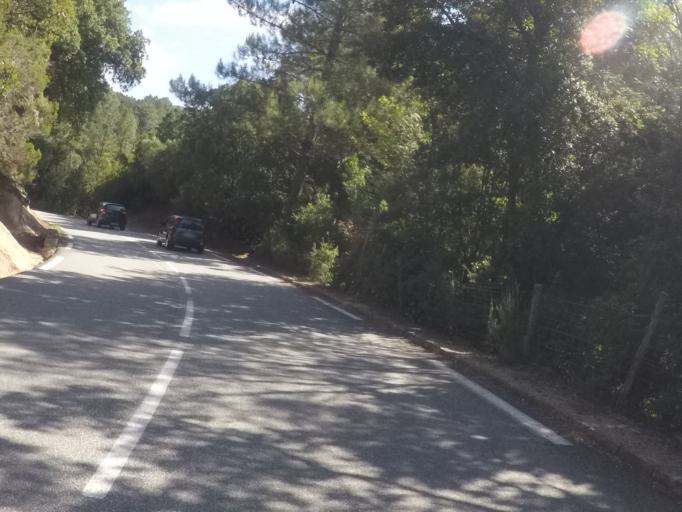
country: FR
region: Corsica
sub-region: Departement de la Corse-du-Sud
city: Zonza
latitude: 41.7679
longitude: 9.1722
